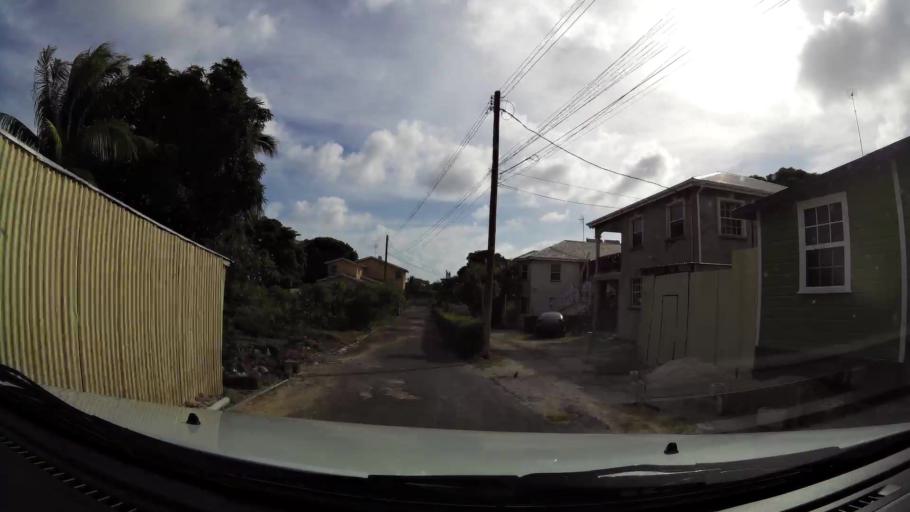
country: BB
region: Saint Michael
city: Bridgetown
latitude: 13.0860
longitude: -59.5829
